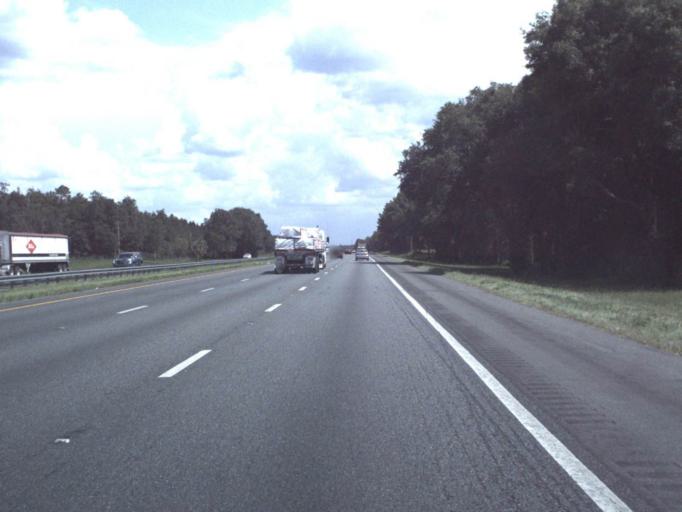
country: US
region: Florida
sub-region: Columbia County
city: Lake City
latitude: 30.1428
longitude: -82.6699
